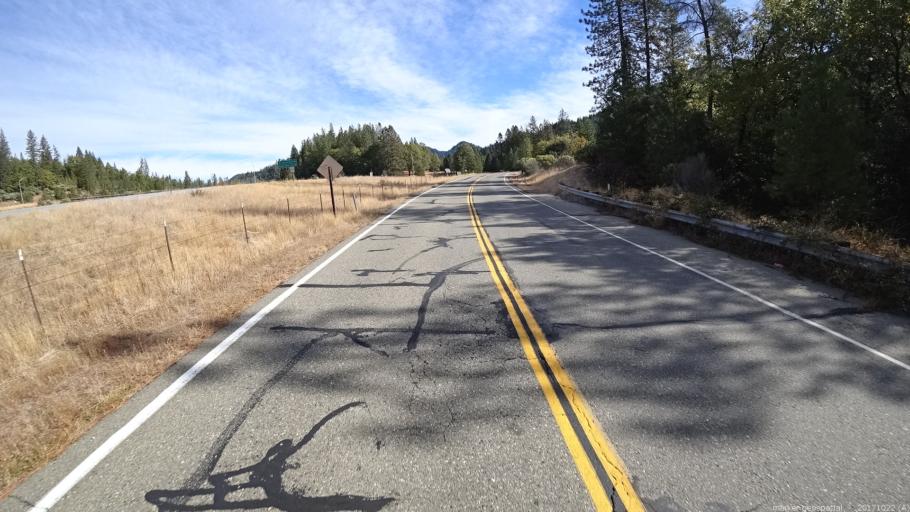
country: US
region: California
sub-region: Siskiyou County
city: Dunsmuir
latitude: 40.9972
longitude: -122.4159
